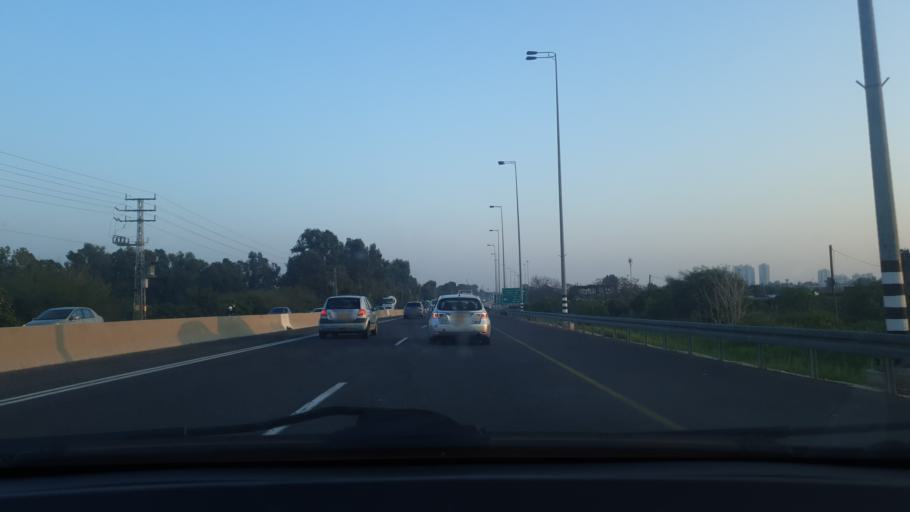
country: IL
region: Central District
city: Ramla
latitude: 31.9572
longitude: 34.8534
